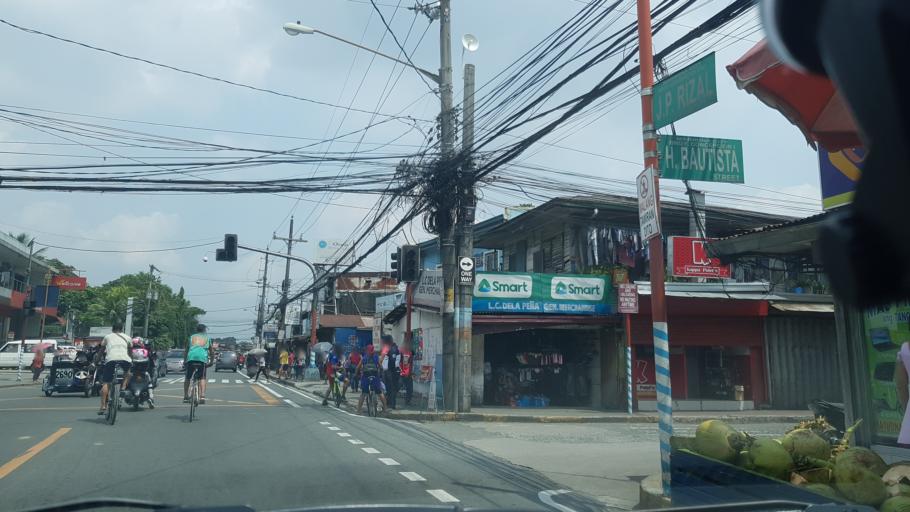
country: PH
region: Metro Manila
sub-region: Marikina
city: Calumpang
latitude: 14.6528
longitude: 121.1032
